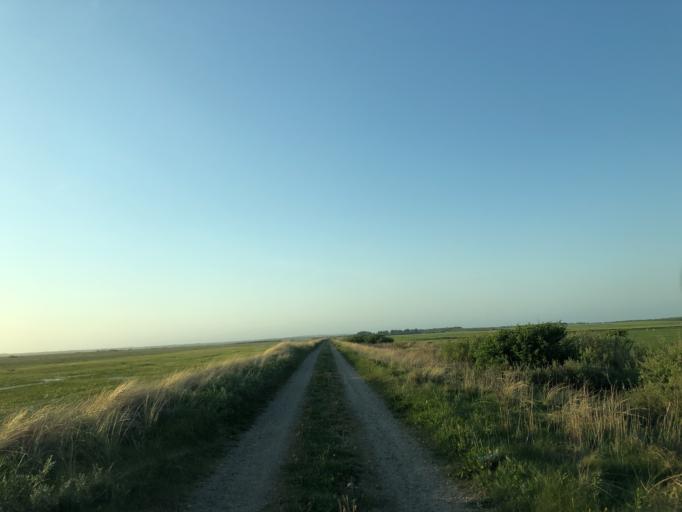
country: DK
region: Central Jutland
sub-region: Ringkobing-Skjern Kommune
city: Ringkobing
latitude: 56.2165
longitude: 8.1651
